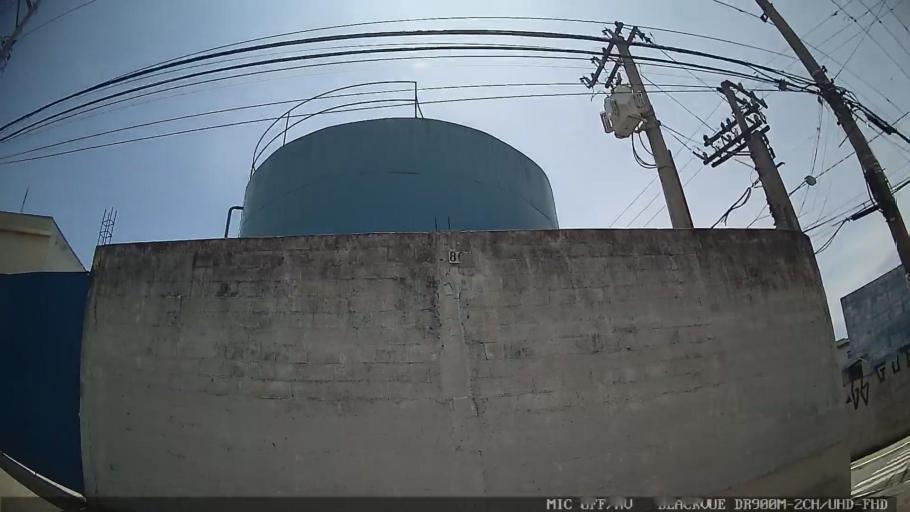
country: BR
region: Sao Paulo
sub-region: Sao Caetano Do Sul
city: Sao Caetano do Sul
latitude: -23.5690
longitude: -46.5571
